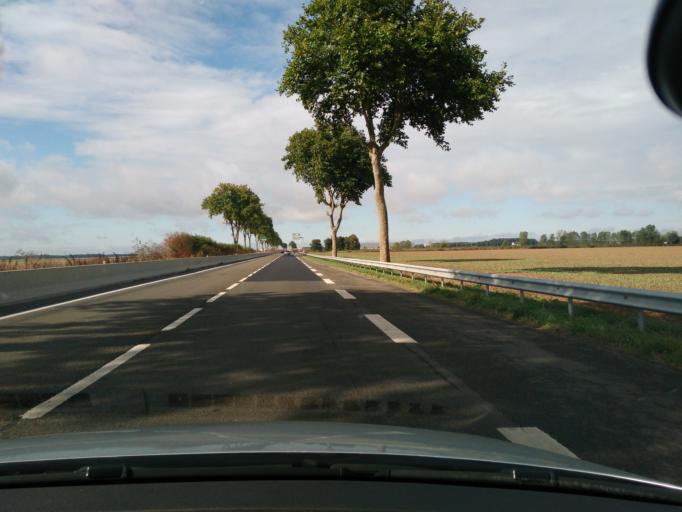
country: FR
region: Centre
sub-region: Departement d'Eure-et-Loir
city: Bu
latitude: 48.7588
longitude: 1.4919
